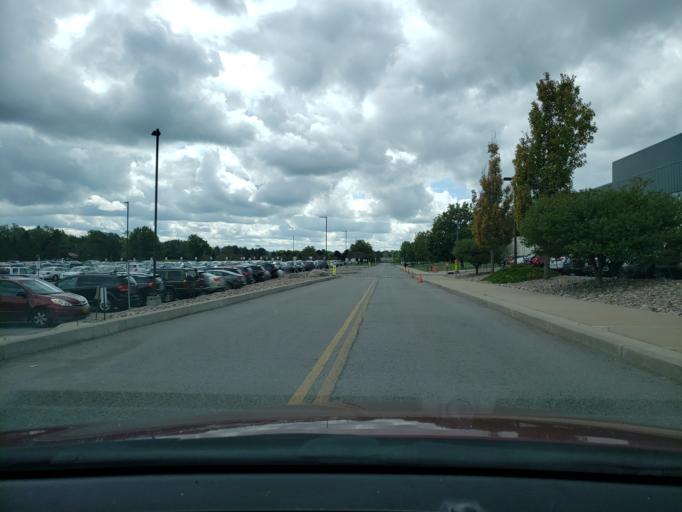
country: US
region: New York
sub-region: Monroe County
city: North Gates
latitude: 43.1515
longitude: -77.7345
